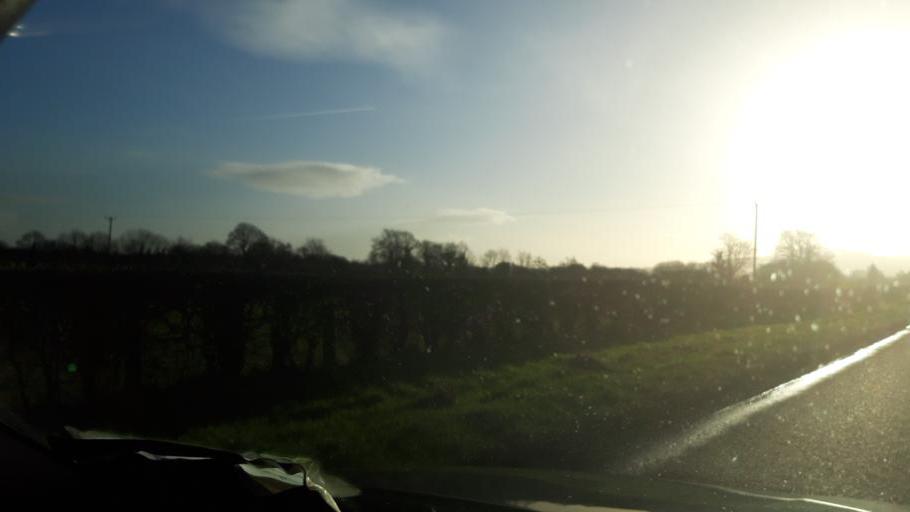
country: GB
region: Northern Ireland
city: Maghera
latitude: 54.8210
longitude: -6.6968
